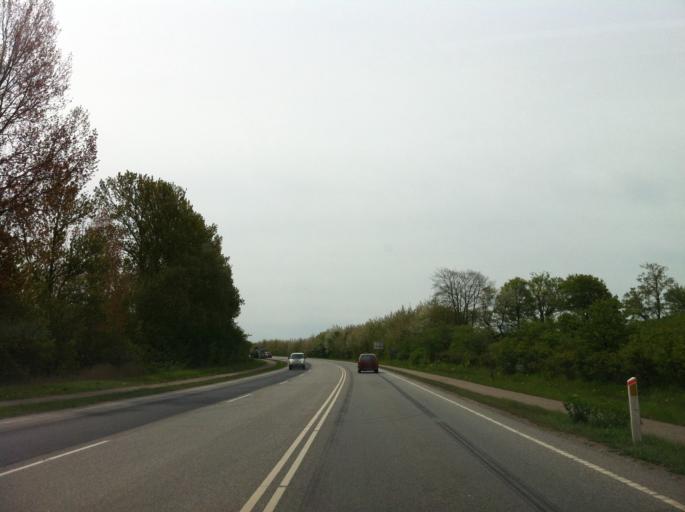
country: DK
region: Zealand
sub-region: Roskilde Kommune
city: Jyllinge
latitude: 55.7189
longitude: 12.1133
